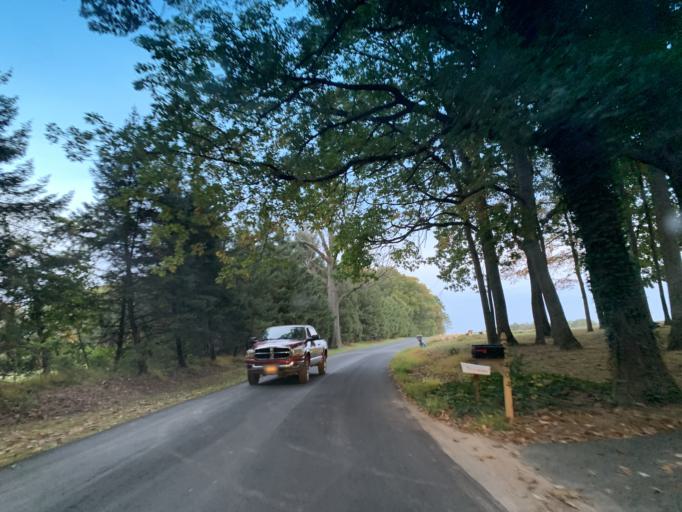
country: US
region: Pennsylvania
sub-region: York County
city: New Freedom
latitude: 39.6840
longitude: -76.6410
